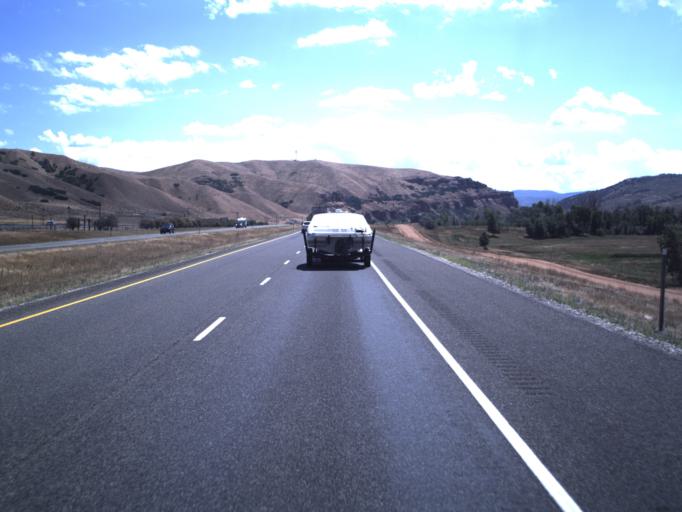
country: US
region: Utah
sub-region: Summit County
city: Coalville
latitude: 40.9929
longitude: -111.4602
